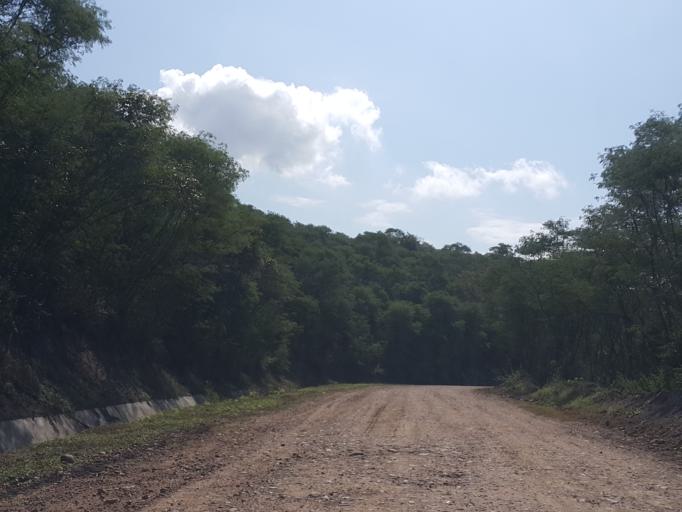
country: TH
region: Lampang
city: Mae Mo
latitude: 18.3288
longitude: 99.7399
